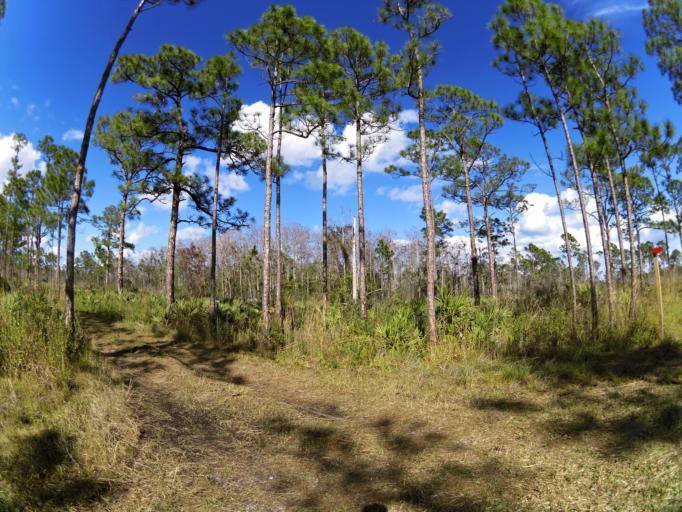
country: US
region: Florida
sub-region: Martin County
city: Hobe Sound
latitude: 27.0205
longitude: -80.1542
